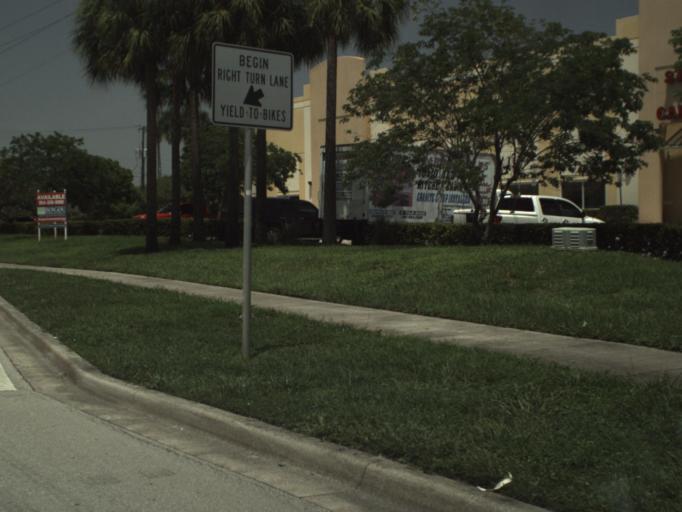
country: US
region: Florida
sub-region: Broward County
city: Tedder
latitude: 26.2965
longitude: -80.1523
